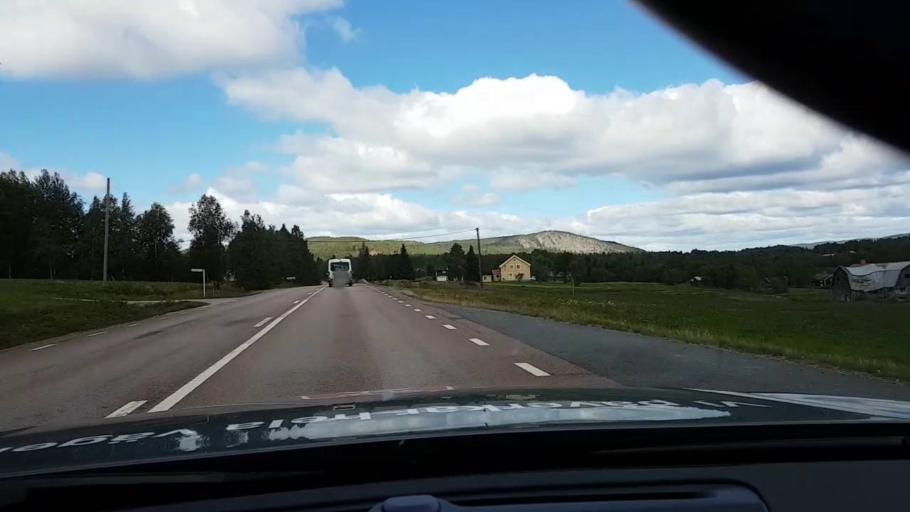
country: SE
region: Vaesternorrland
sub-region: OErnskoeldsviks Kommun
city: Bjasta
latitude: 63.3697
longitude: 18.4404
